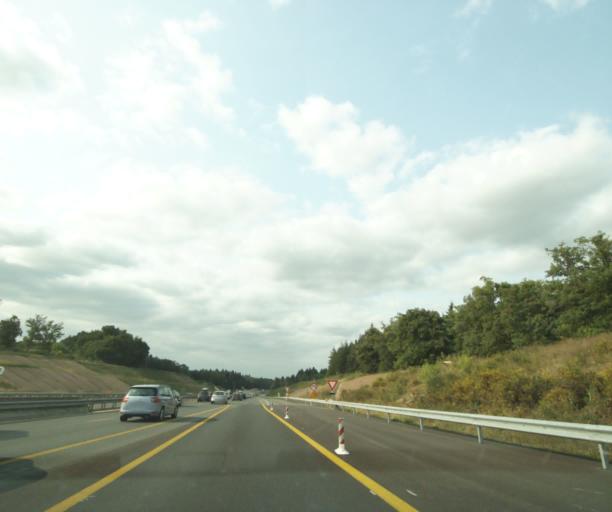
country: FR
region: Centre
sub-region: Departement d'Indre-et-Loire
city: Montbazon
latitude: 47.3066
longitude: 0.6919
